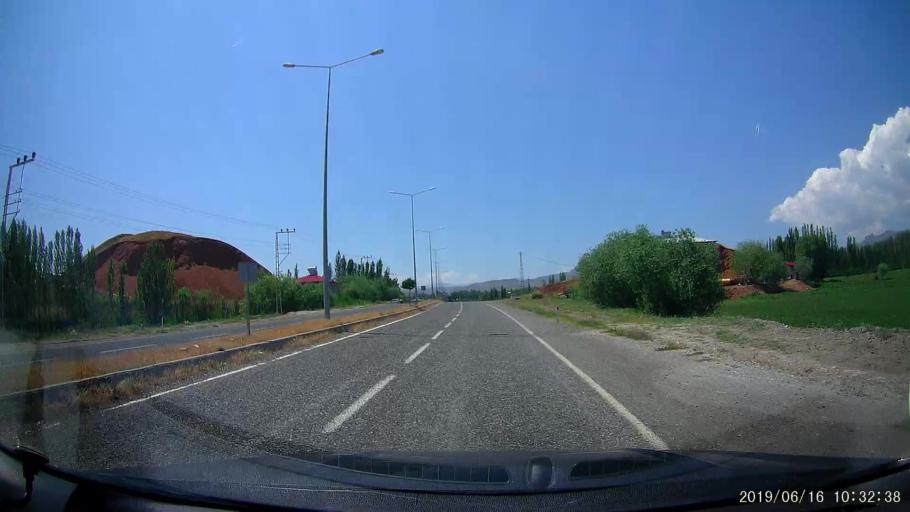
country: TR
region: Igdir
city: Tuzluca
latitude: 40.0488
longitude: 43.6540
